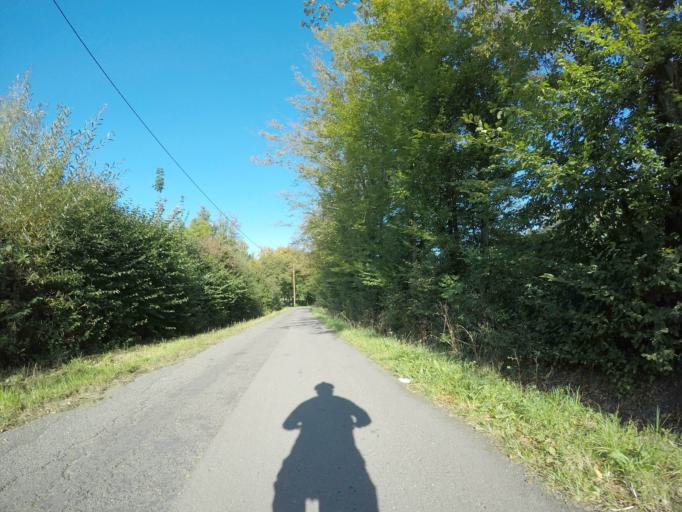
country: DE
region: Baden-Wuerttemberg
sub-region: Tuebingen Region
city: Reutlingen
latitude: 48.4722
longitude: 9.1894
